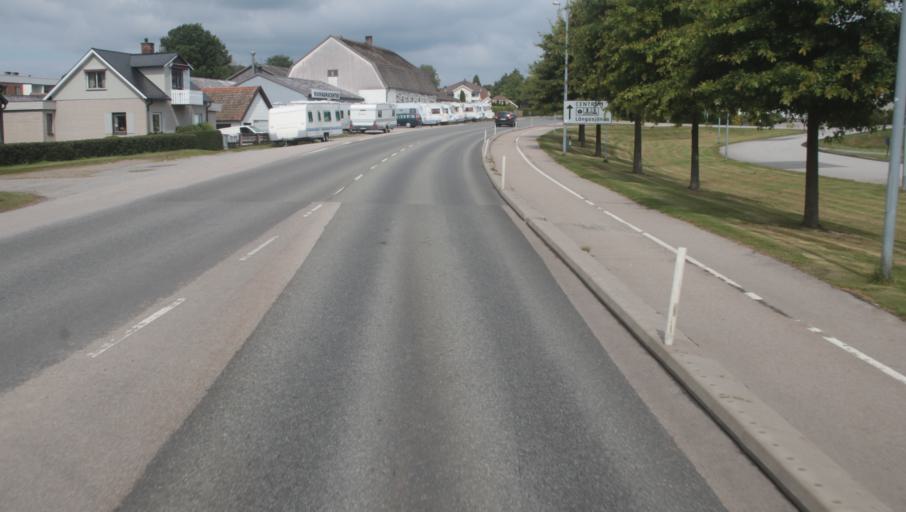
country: SE
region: Blekinge
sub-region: Karlshamns Kommun
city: Karlshamn
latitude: 56.2008
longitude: 14.8359
